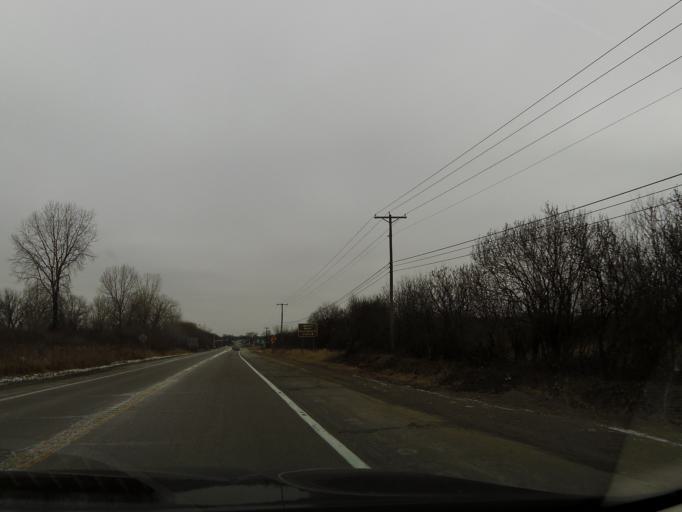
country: US
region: Minnesota
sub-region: Hennepin County
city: Maple Plain
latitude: 45.0019
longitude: -93.6411
